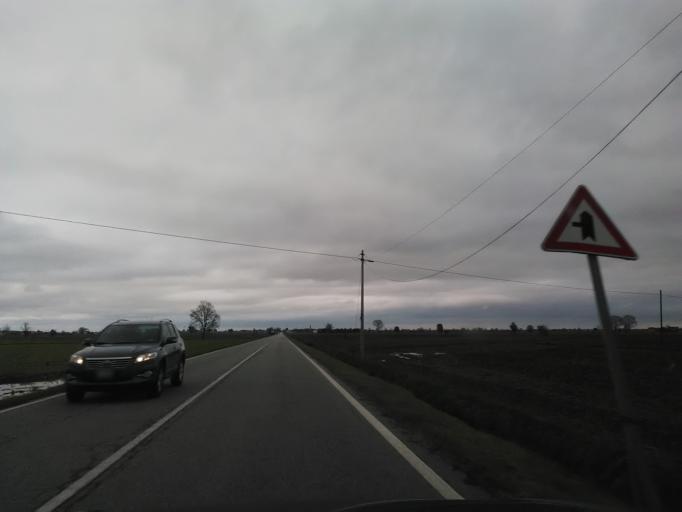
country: IT
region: Piedmont
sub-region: Provincia di Vercelli
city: Bianze
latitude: 45.3343
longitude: 8.1325
